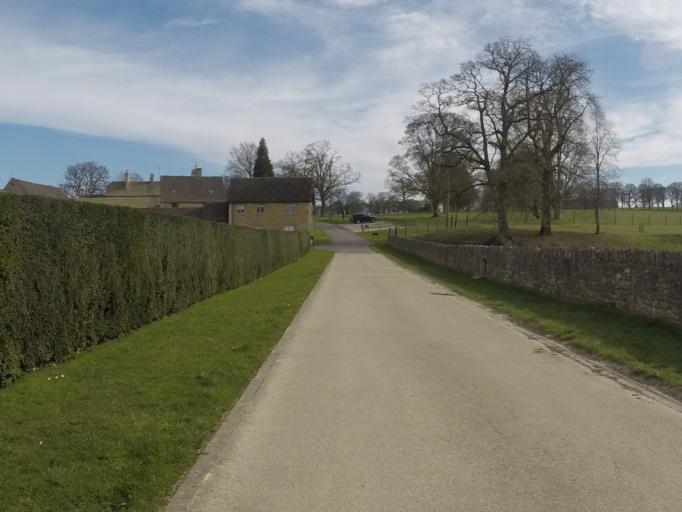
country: GB
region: England
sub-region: Oxfordshire
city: Charlbury
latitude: 51.8589
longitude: -1.4821
